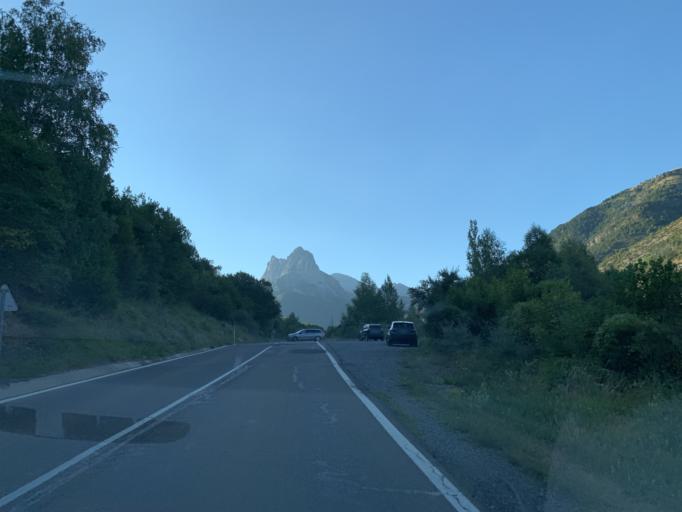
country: ES
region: Aragon
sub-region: Provincia de Huesca
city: Sallent de Gallego
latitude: 42.7512
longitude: -0.3168
